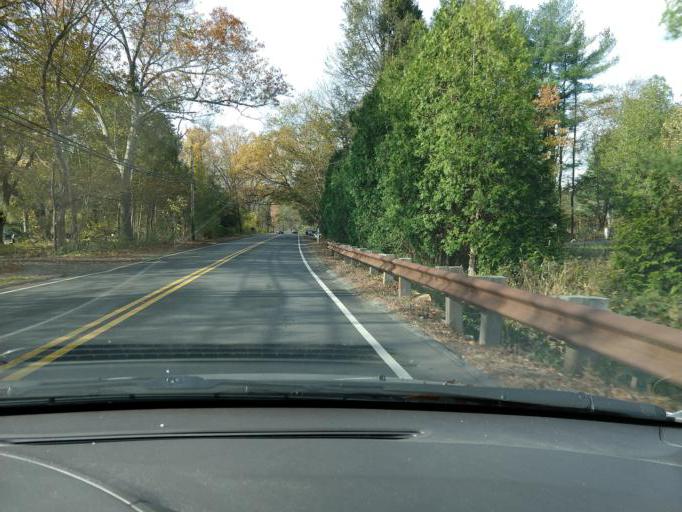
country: US
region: Massachusetts
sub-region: Middlesex County
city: Concord
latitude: 42.4736
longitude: -71.3696
